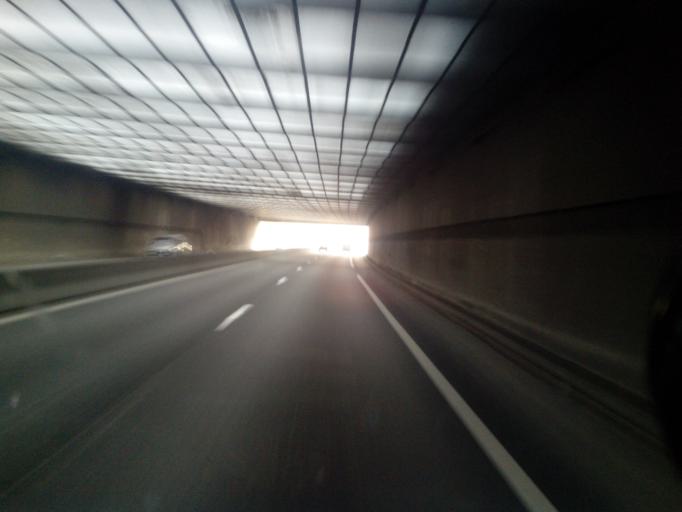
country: FR
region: Limousin
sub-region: Departement de la Haute-Vienne
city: Limoges
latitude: 45.8269
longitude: 1.2839
